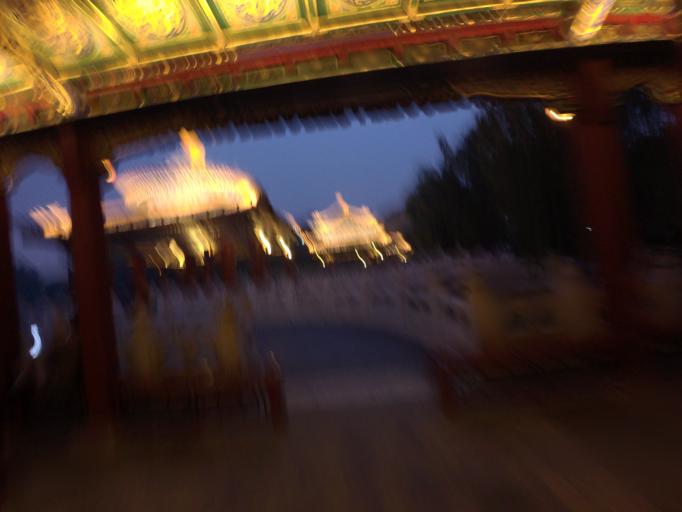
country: CN
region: Beijing
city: Jingshan
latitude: 39.9286
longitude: 116.3802
